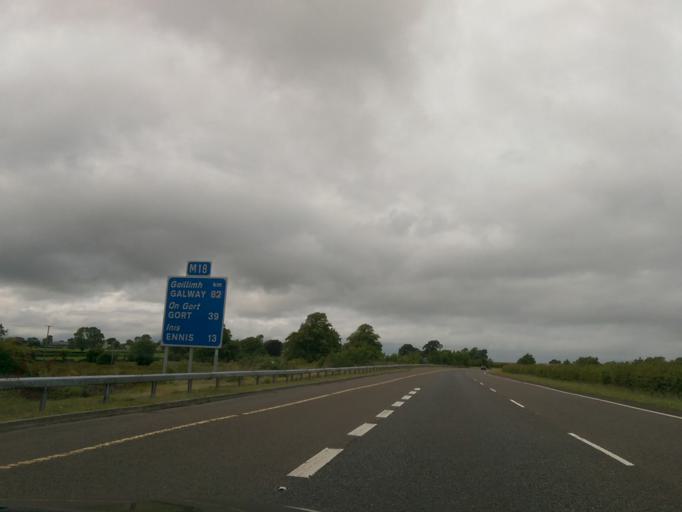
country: IE
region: Munster
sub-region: An Clar
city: Newmarket on Fergus
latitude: 52.7552
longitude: -8.9101
